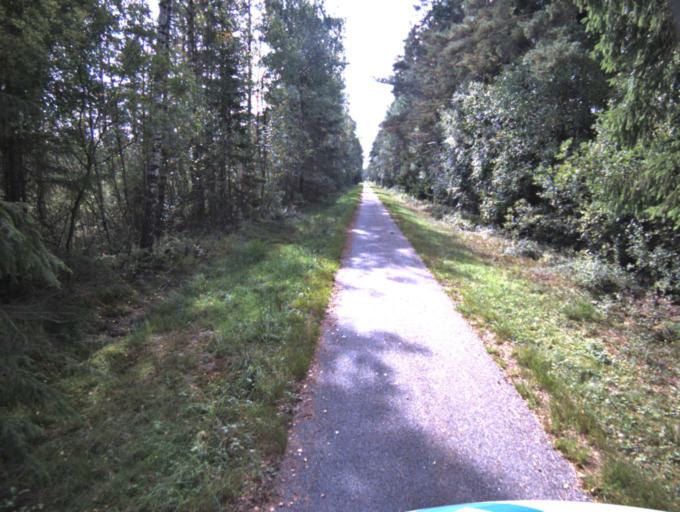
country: SE
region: Vaestra Goetaland
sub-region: Tranemo Kommun
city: Limmared
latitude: 57.6190
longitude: 13.3445
